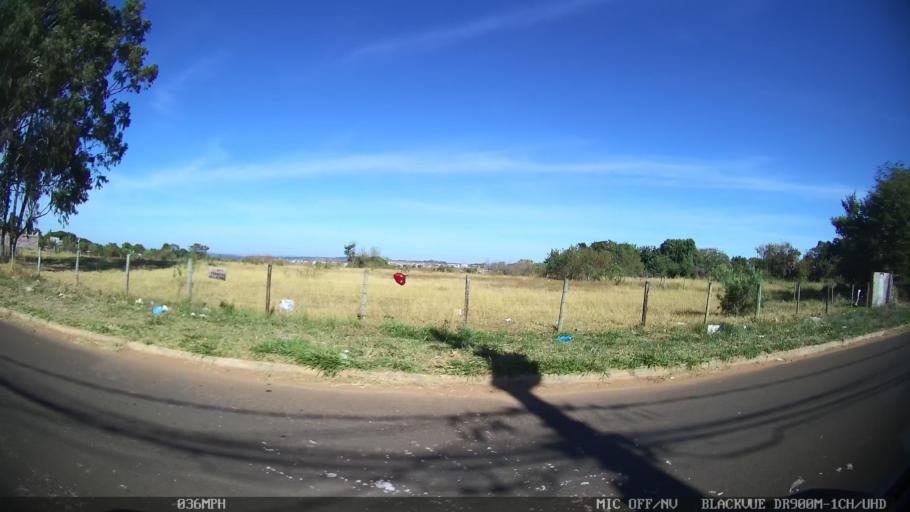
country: BR
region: Sao Paulo
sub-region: Franca
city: Franca
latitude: -20.5660
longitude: -47.3544
